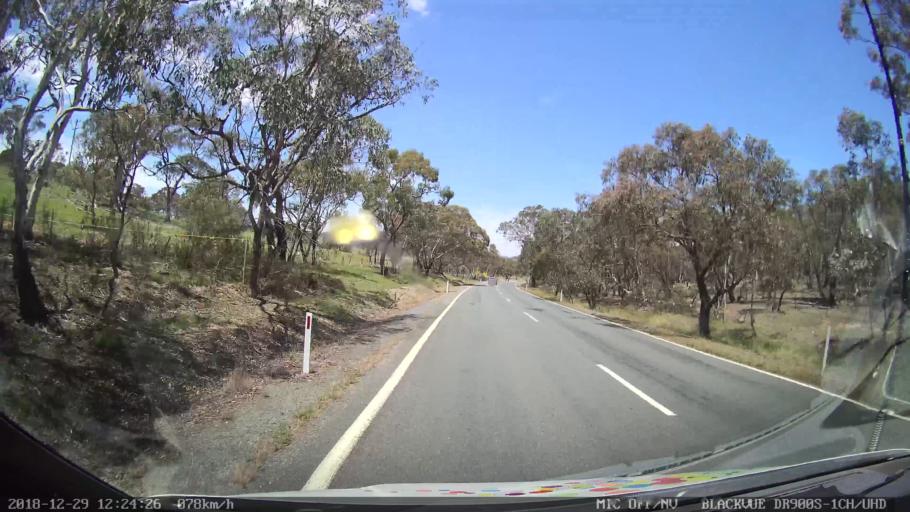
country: AU
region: Australian Capital Territory
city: Macarthur
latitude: -35.4469
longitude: 149.2111
